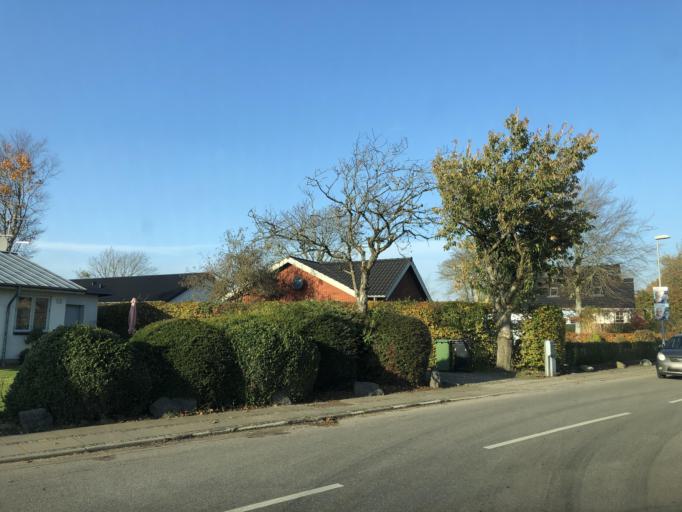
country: DK
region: Central Jutland
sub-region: Holstebro Kommune
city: Vinderup
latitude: 56.4026
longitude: 8.7521
